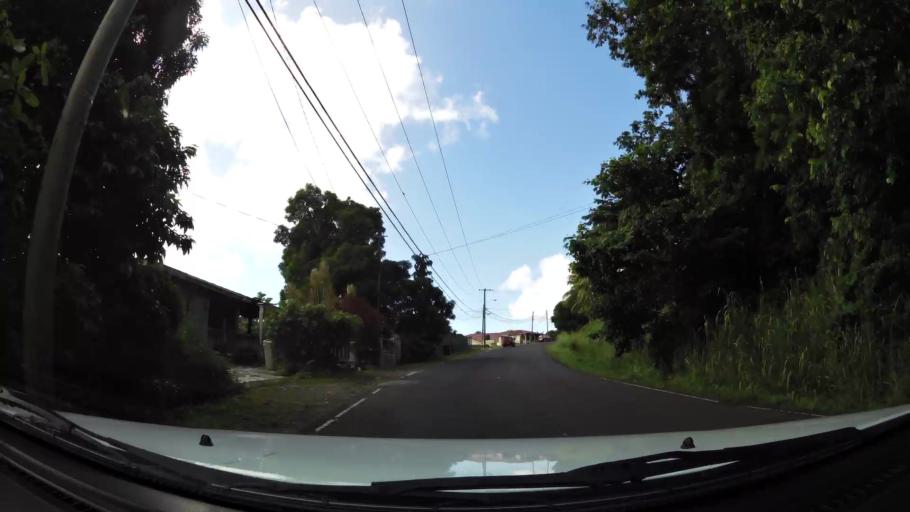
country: LC
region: Castries Quarter
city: Castries
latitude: 13.9931
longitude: -60.9986
